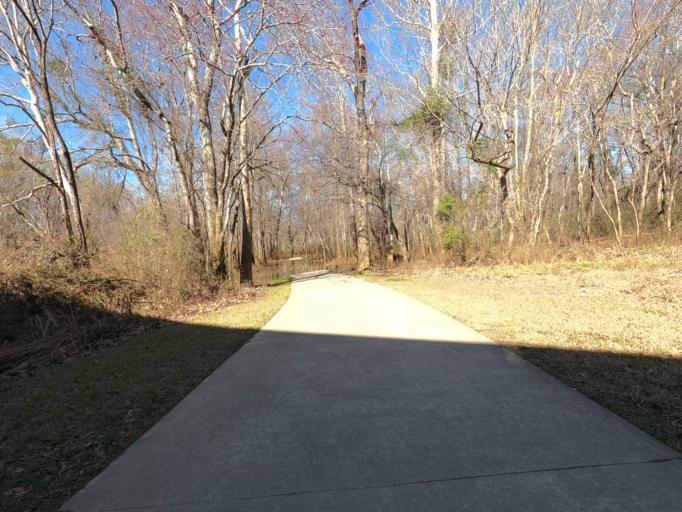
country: US
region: Georgia
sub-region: Clarke County
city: Athens
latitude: 33.9770
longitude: -83.3819
